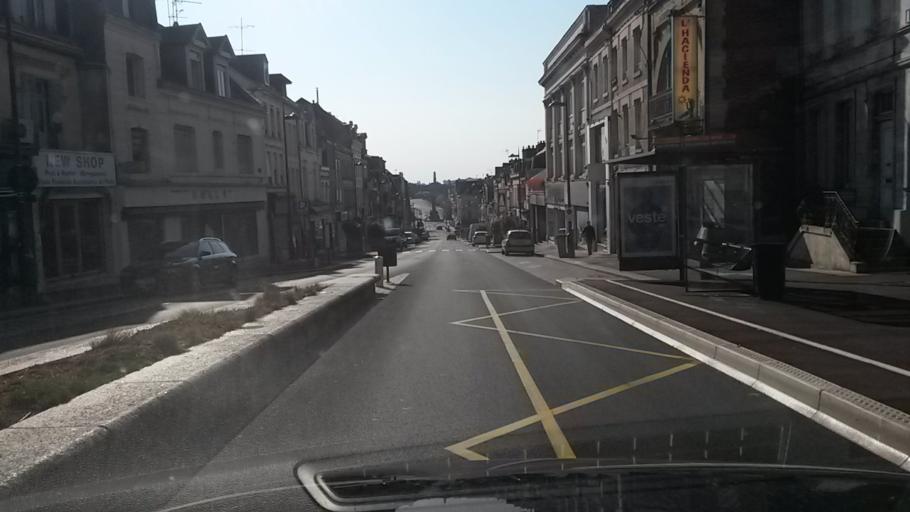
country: FR
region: Picardie
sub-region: Departement de l'Aisne
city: Saint-Quentin
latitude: 49.8440
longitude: 3.2916
